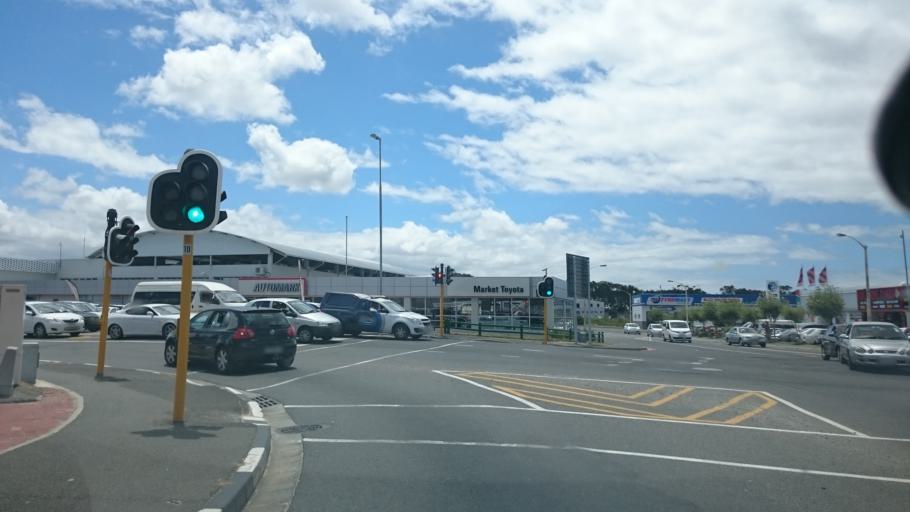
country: ZA
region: Western Cape
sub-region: City of Cape Town
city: Bergvliet
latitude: -34.0659
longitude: 18.4586
